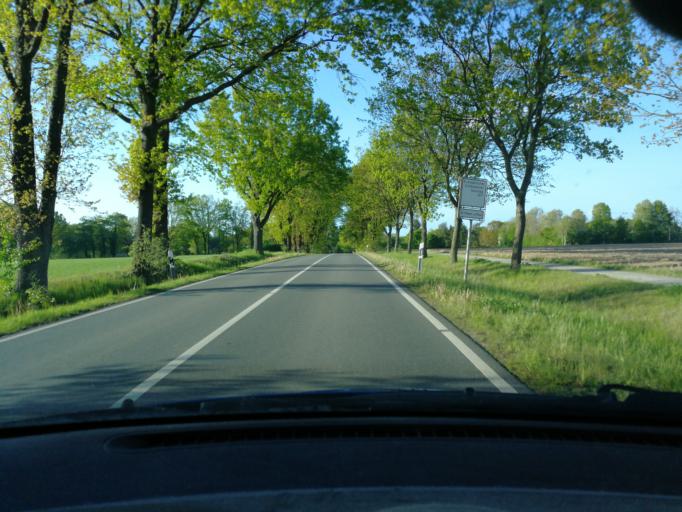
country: DE
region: Lower Saxony
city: Betzendorf
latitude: 53.1328
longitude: 10.3094
